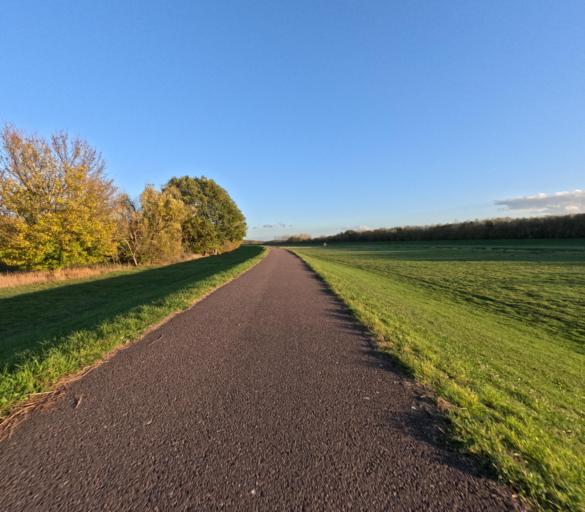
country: DE
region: Saxony-Anhalt
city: Ermlitz
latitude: 51.3849
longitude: 12.1370
